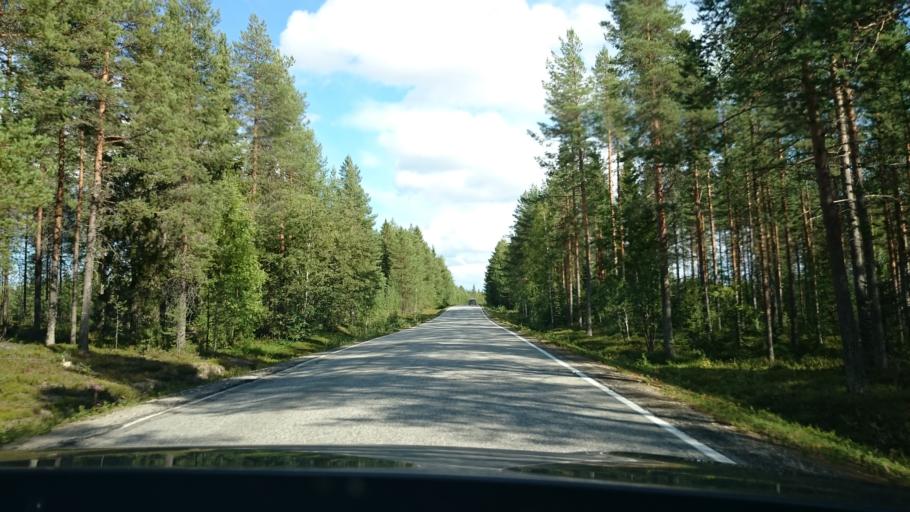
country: FI
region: Kainuu
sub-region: Kehys-Kainuu
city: Suomussalmi
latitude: 64.7566
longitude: 29.4034
